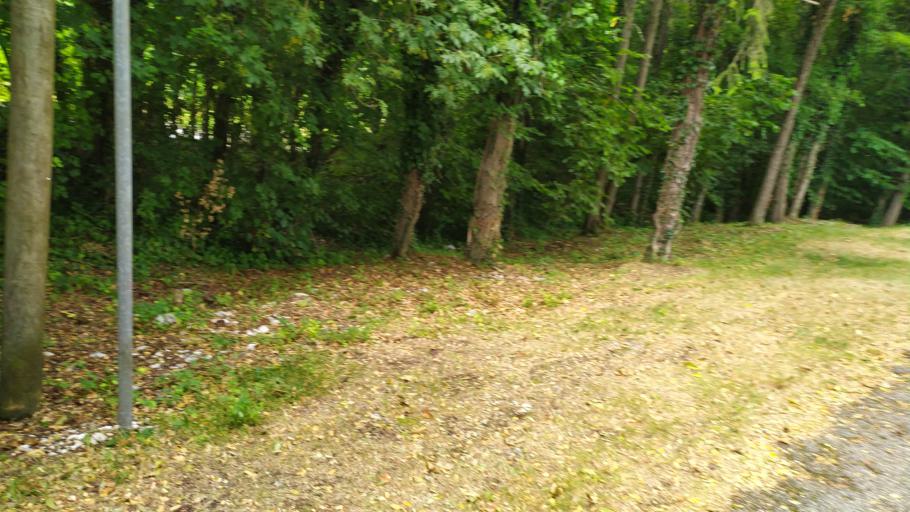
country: IT
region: Friuli Venezia Giulia
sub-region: Provincia di Pordenone
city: Polcenigo
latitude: 46.0226
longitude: 12.4779
